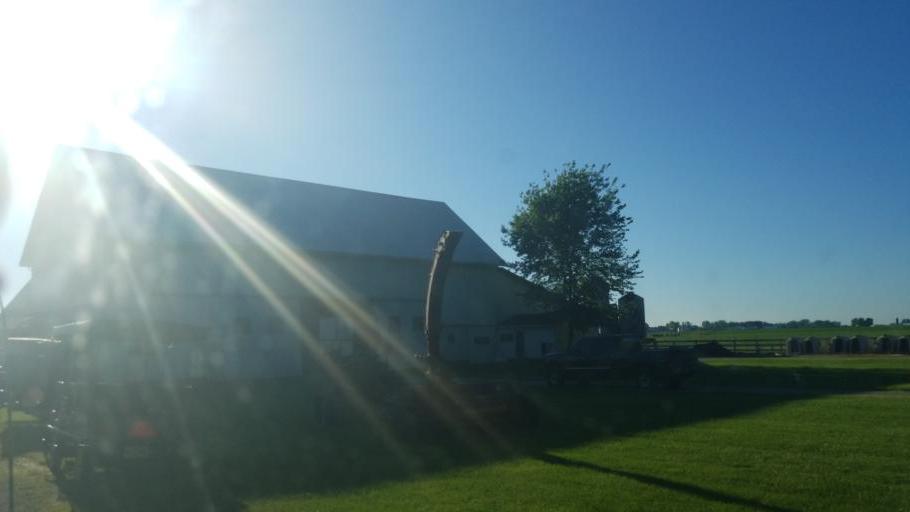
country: US
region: Indiana
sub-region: Marshall County
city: Bremen
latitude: 41.4166
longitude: -86.0975
